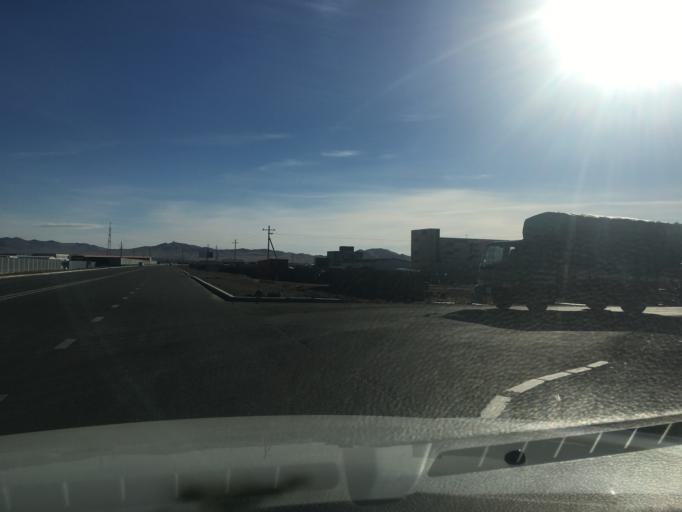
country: MN
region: Ulaanbaatar
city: Ulaanbaatar
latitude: 47.8975
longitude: 106.7060
